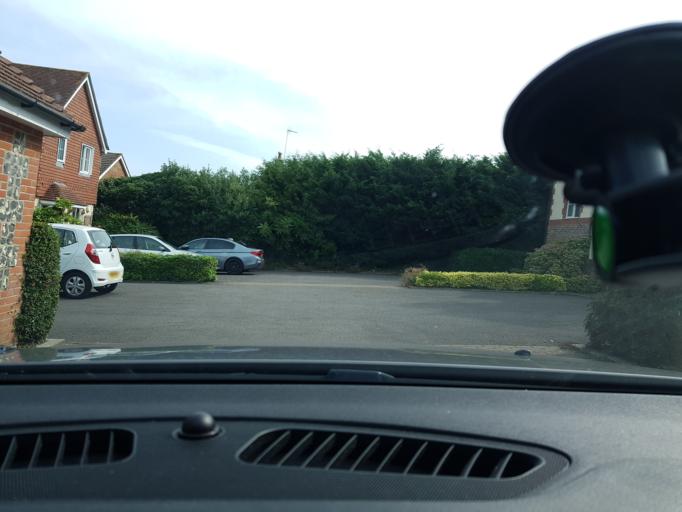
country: GB
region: England
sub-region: West Berkshire
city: Hungerford
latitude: 51.4141
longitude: -1.5185
